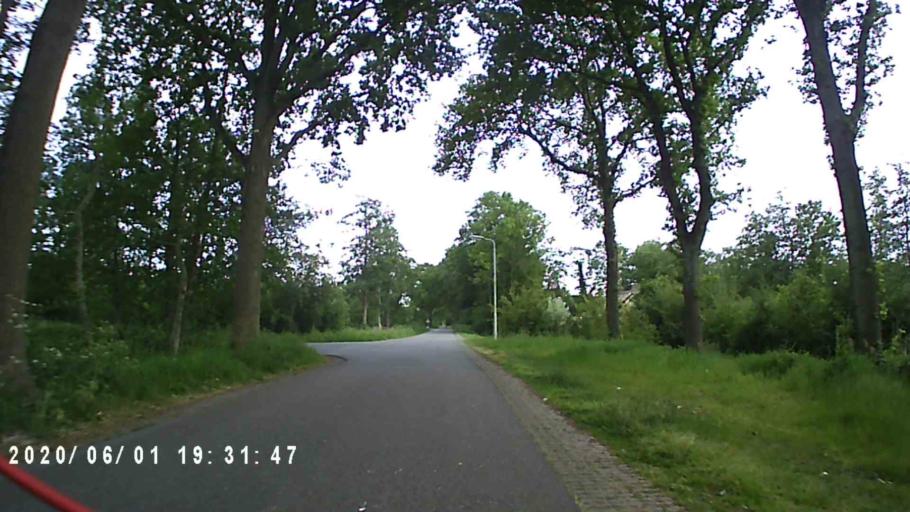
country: NL
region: Friesland
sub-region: Gemeente Achtkarspelen
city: Augustinusga
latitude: 53.2139
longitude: 6.1574
